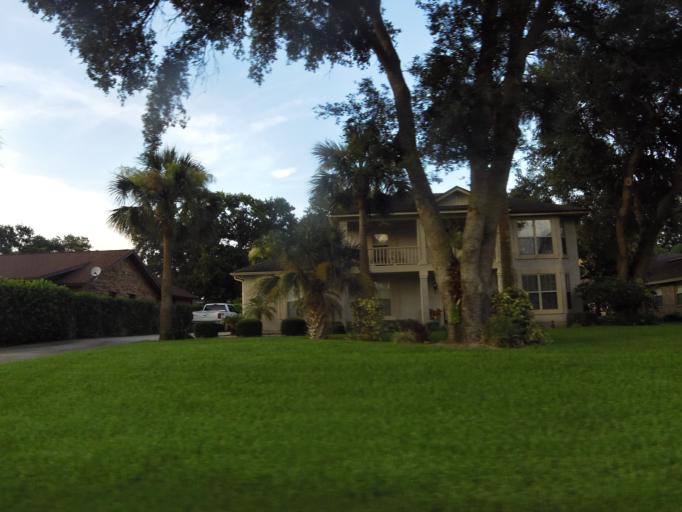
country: US
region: Florida
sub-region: Duval County
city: Atlantic Beach
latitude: 30.3943
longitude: -81.5021
